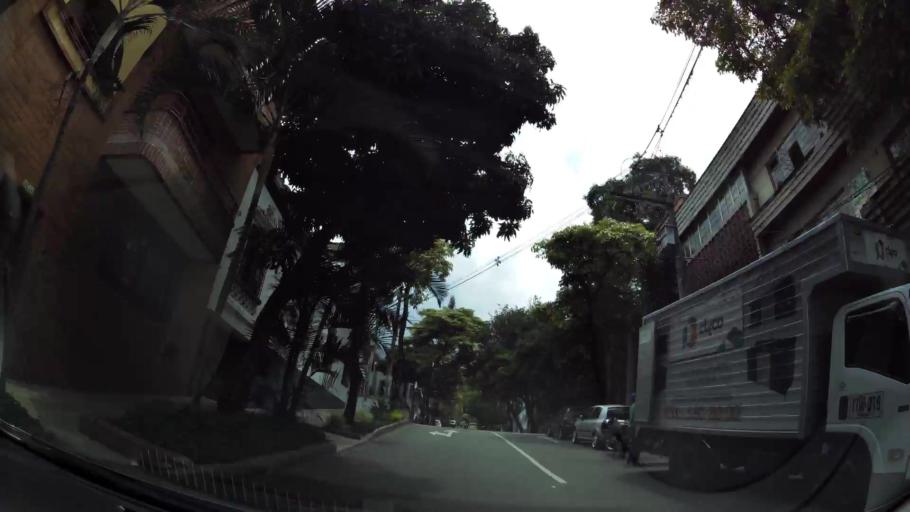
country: CO
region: Antioquia
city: Medellin
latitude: 6.2613
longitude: -75.5632
